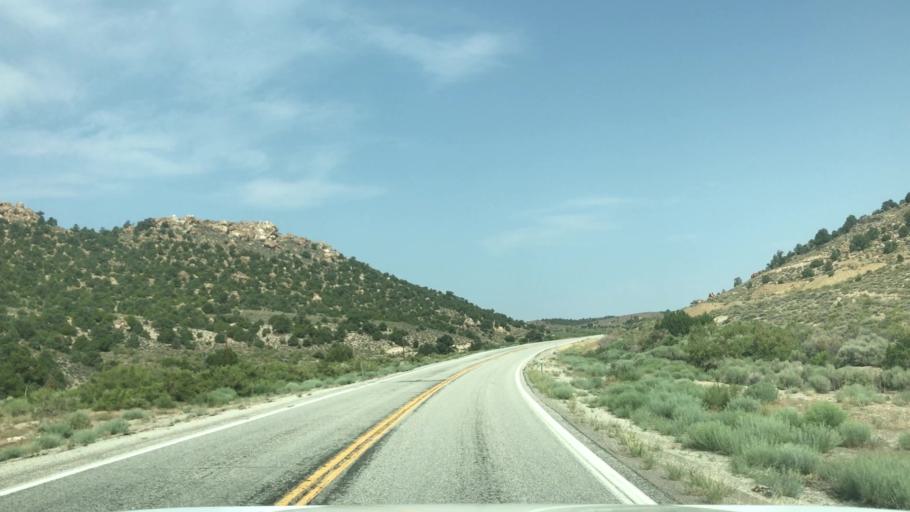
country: US
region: Nevada
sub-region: White Pine County
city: McGill
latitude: 39.1168
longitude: -114.2825
